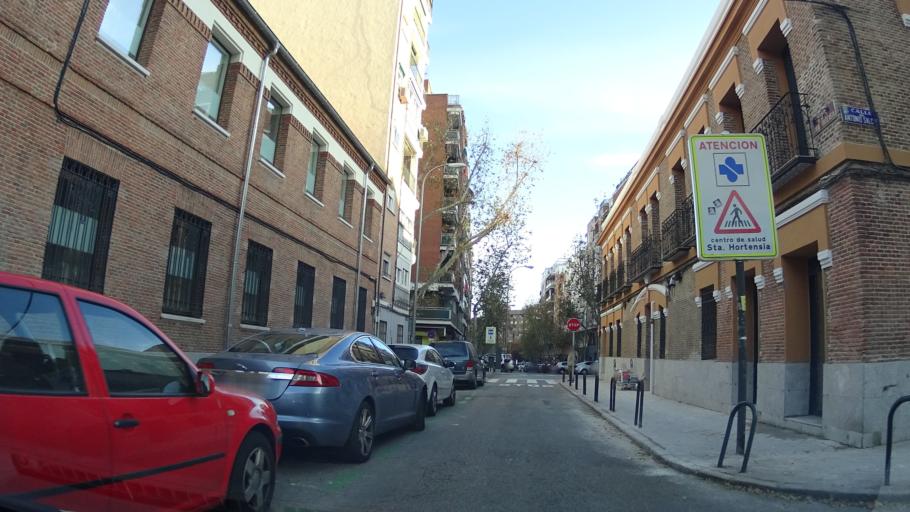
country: ES
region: Madrid
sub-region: Provincia de Madrid
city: Chamartin
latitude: 40.4456
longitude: -3.6700
